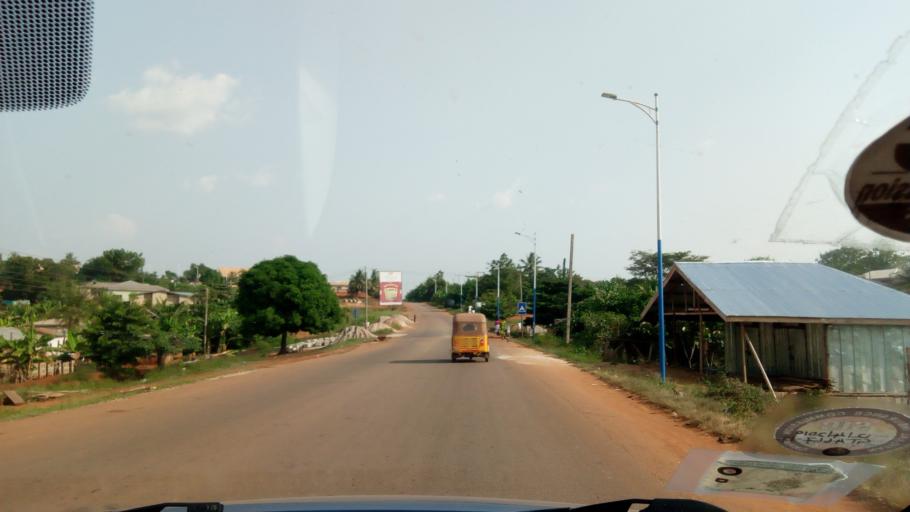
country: GH
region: Western
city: Bibiani
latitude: 6.8081
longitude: -2.5288
